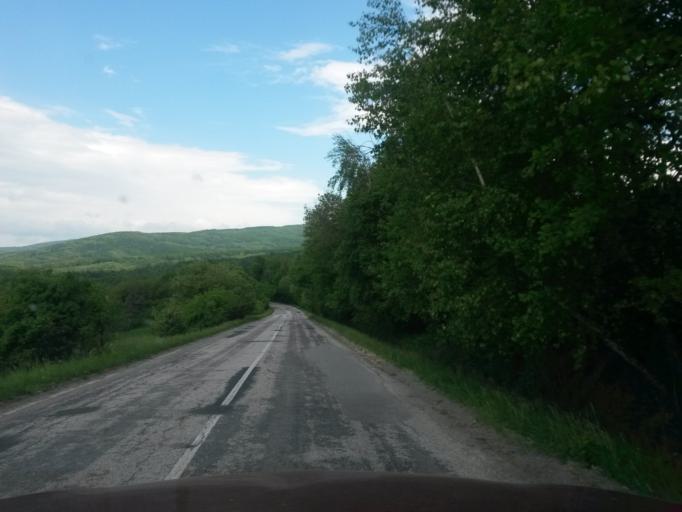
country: SK
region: Kosicky
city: Moldava nad Bodvou
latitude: 48.7302
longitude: 21.0983
